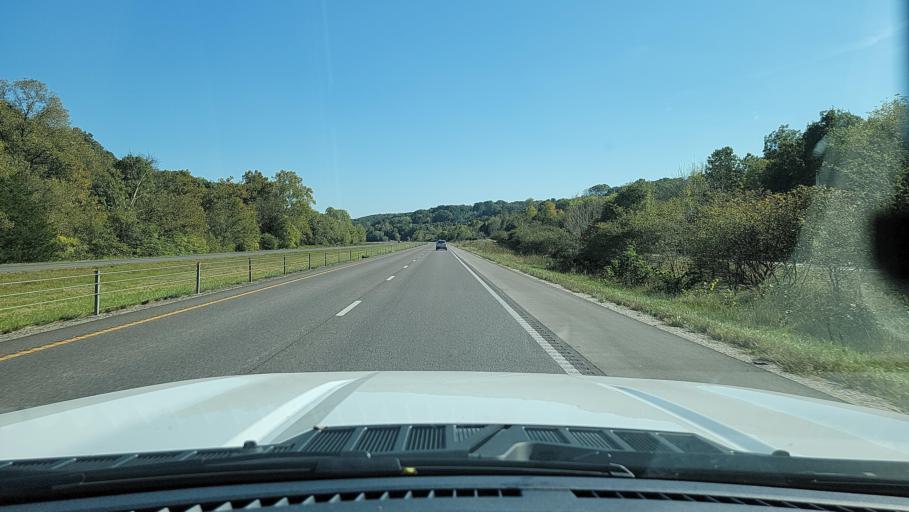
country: US
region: Missouri
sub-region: Sainte Genevieve County
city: Sainte Genevieve
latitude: 37.9062
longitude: -90.0715
